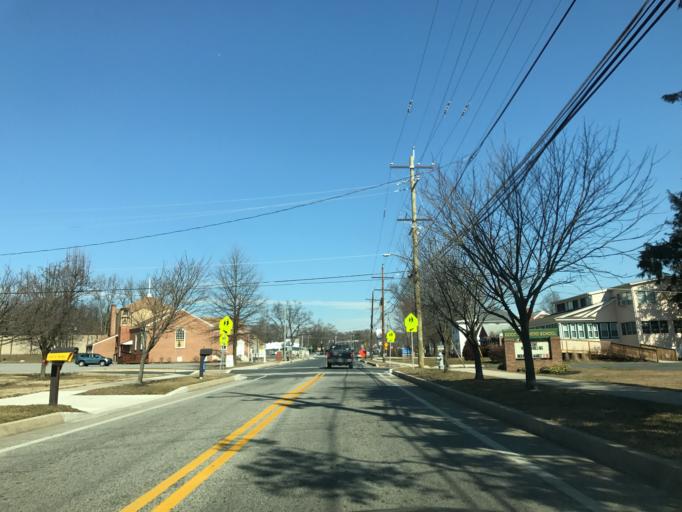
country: US
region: Maryland
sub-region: Cecil County
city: Perryville
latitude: 39.5673
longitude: -76.0707
